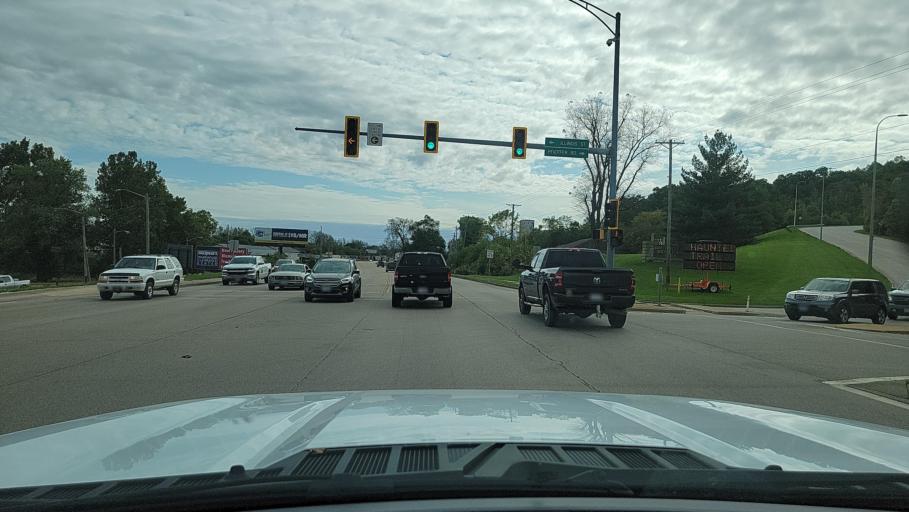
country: US
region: Illinois
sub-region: Peoria County
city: Bartonville
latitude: 40.6393
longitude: -89.6521
